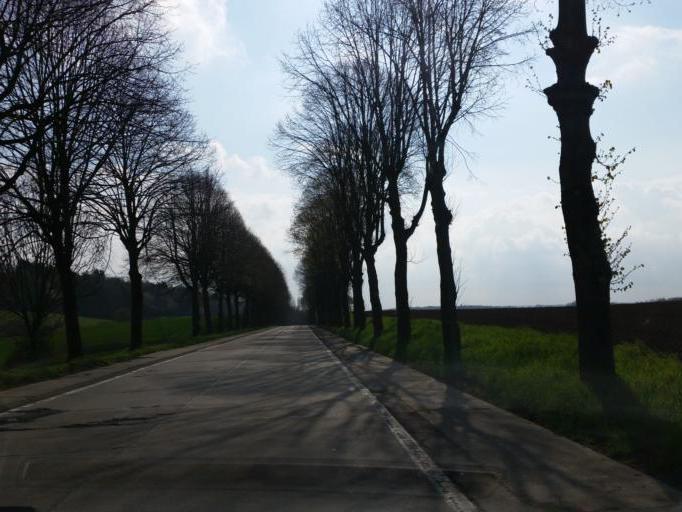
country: BE
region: Flanders
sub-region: Provincie Vlaams-Brabant
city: Bertem
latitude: 50.8675
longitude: 4.6028
